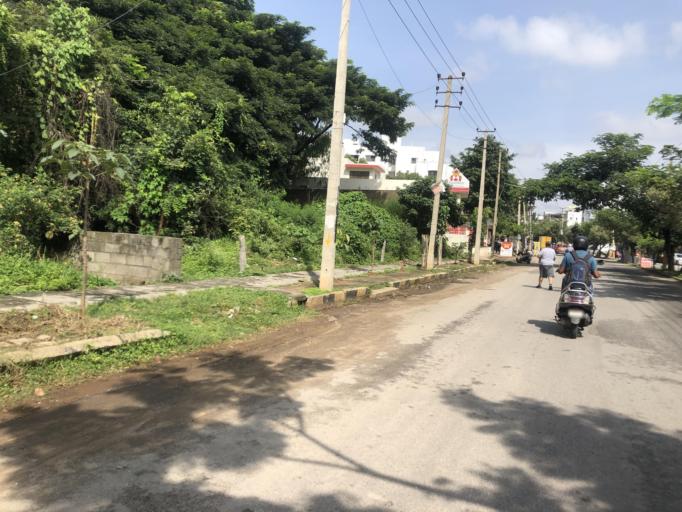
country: IN
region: Karnataka
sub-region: Bangalore Urban
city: Bangalore
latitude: 12.9144
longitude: 77.5237
